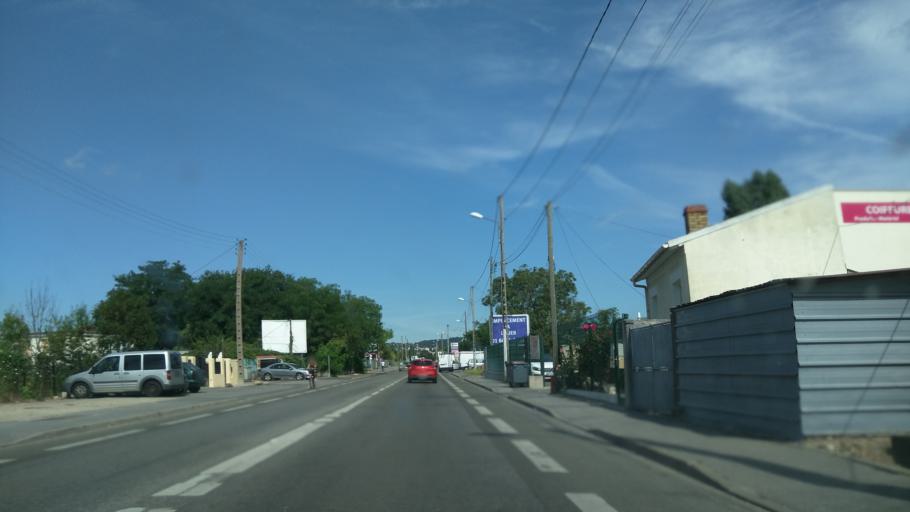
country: FR
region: Ile-de-France
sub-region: Departement des Yvelines
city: Sartrouville
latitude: 48.9516
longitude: 2.2058
